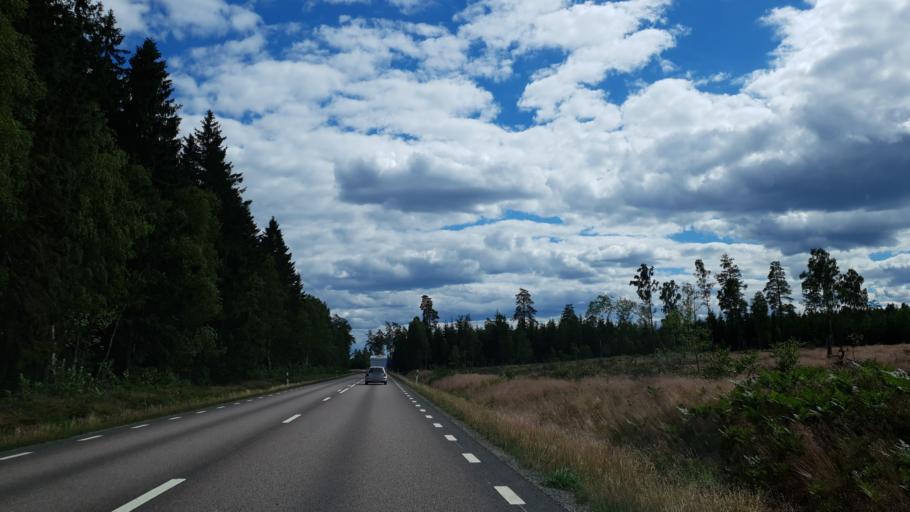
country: SE
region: Kronoberg
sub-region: Lessebo Kommun
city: Lessebo
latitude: 56.8378
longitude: 15.3920
